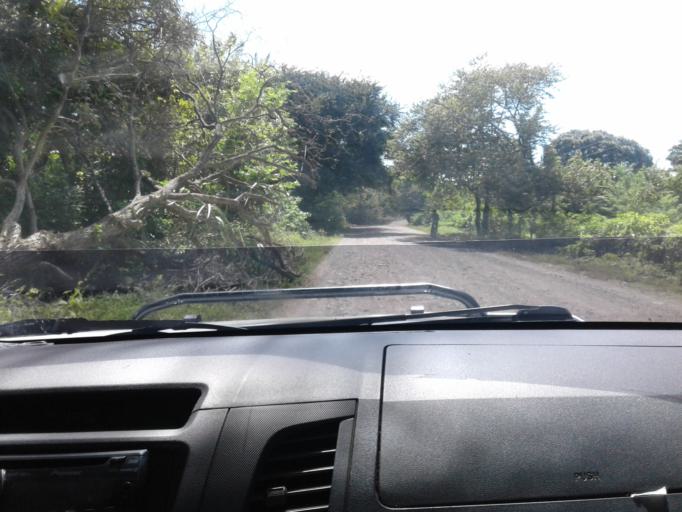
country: NI
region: Rivas
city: Altagracia
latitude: 11.4670
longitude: -85.5587
